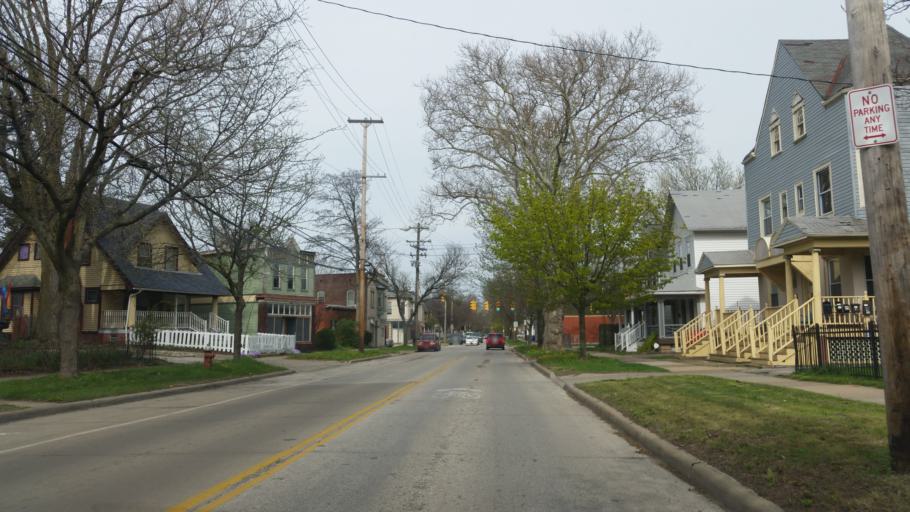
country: US
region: Ohio
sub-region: Cuyahoga County
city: Cleveland
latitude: 41.4833
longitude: -81.7248
